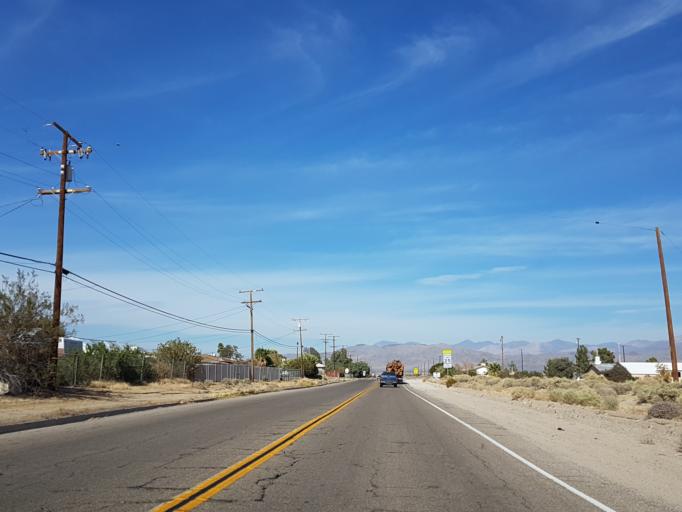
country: US
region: California
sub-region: San Bernardino County
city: Searles Valley
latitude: 35.7895
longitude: -117.3594
